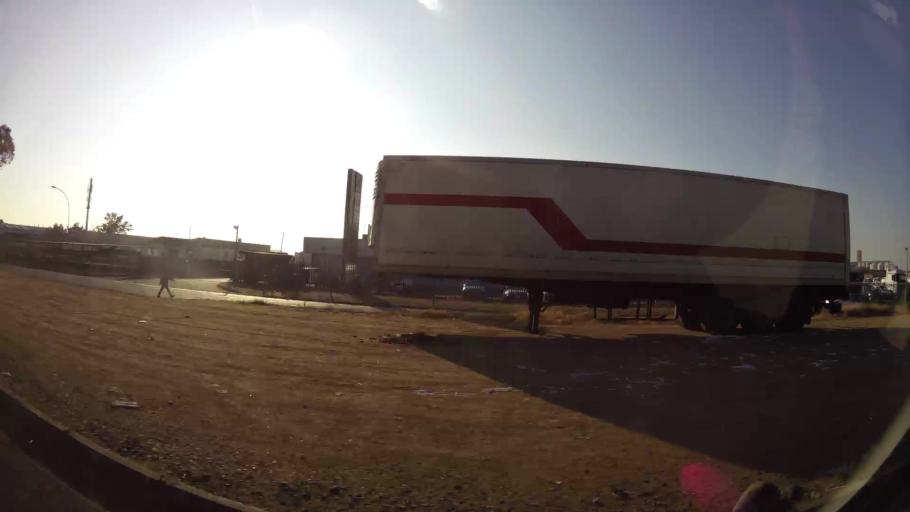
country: ZA
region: Orange Free State
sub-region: Mangaung Metropolitan Municipality
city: Bloemfontein
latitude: -29.1574
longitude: 26.2187
